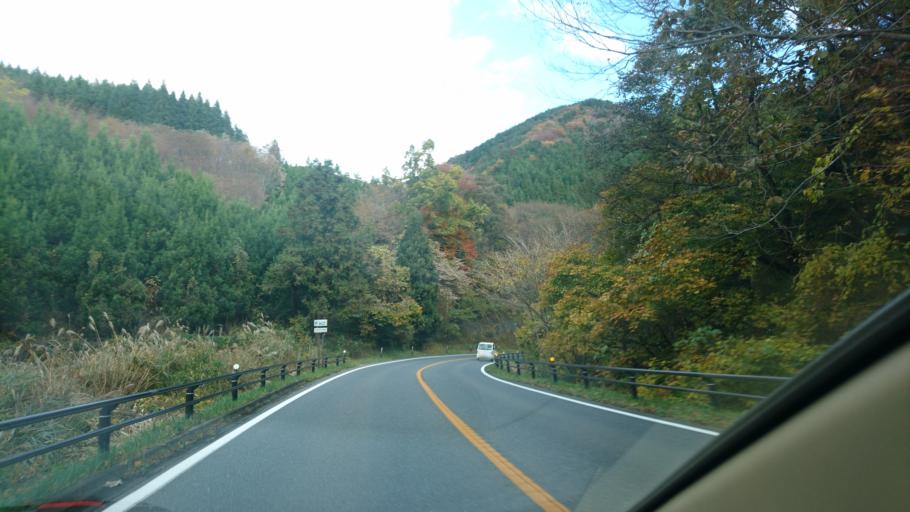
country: JP
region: Iwate
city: Ofunato
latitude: 39.0275
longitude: 141.6956
